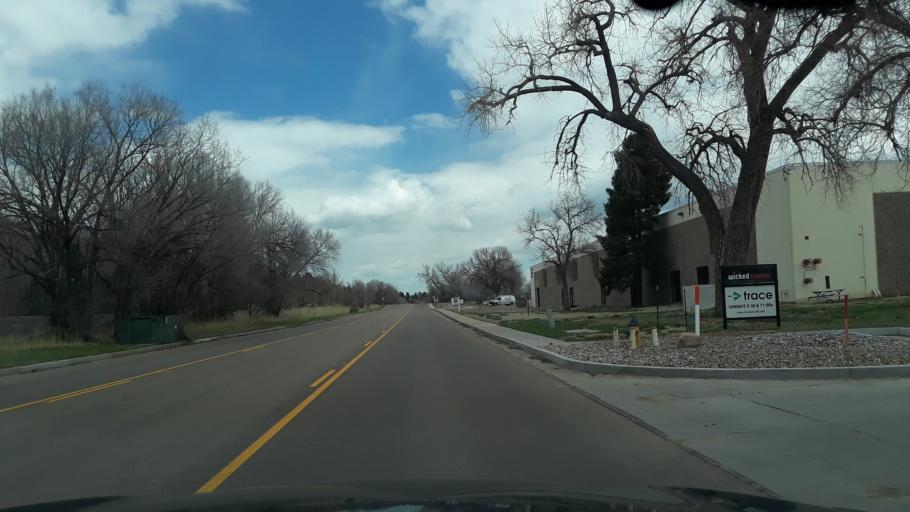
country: US
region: Colorado
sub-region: El Paso County
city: Colorado Springs
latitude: 38.9164
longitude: -104.8214
